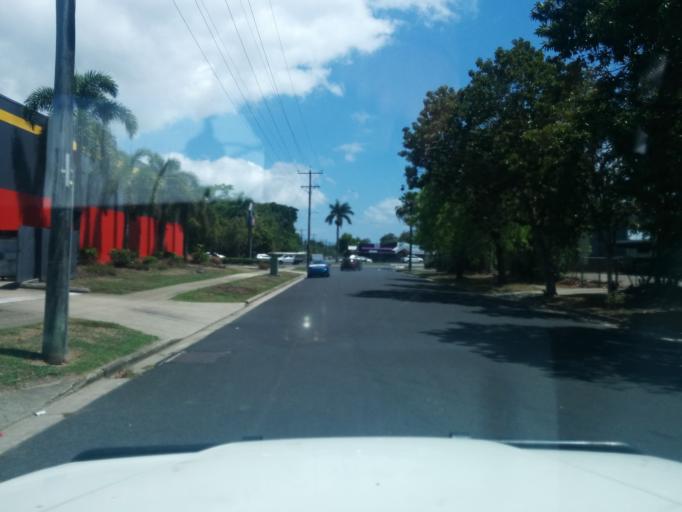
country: AU
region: Queensland
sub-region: Cairns
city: Cairns
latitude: -16.9159
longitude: 145.7430
